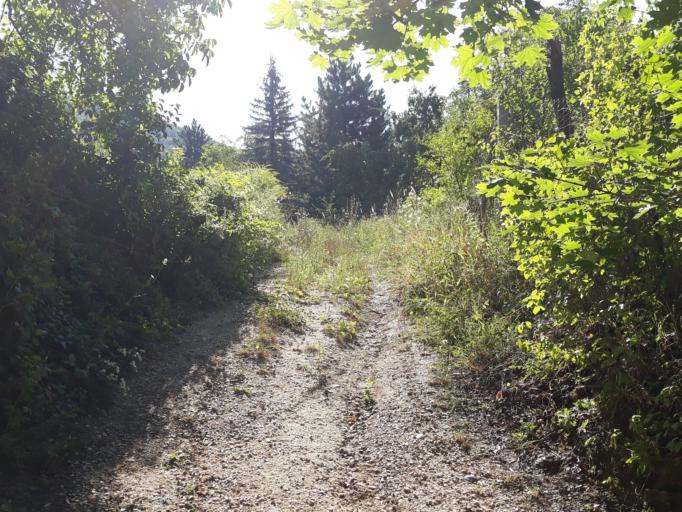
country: HU
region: Komarom-Esztergom
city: Esztergom
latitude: 47.7845
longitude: 18.7659
